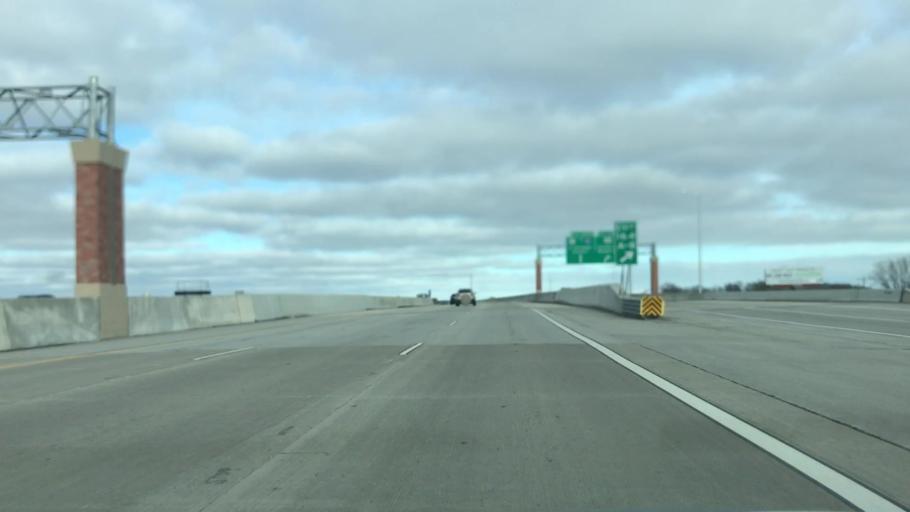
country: US
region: Wisconsin
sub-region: Brown County
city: Ashwaubenon
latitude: 44.4647
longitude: -88.0814
